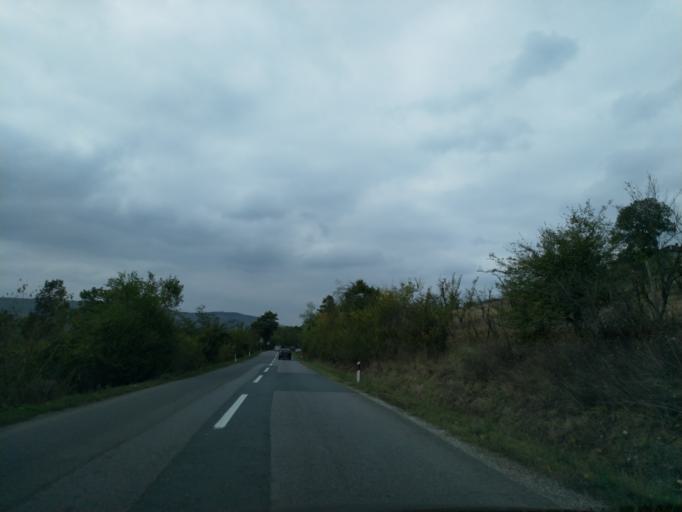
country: RS
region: Central Serbia
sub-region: Sumadijski Okrug
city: Topola
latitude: 44.2260
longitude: 20.7139
